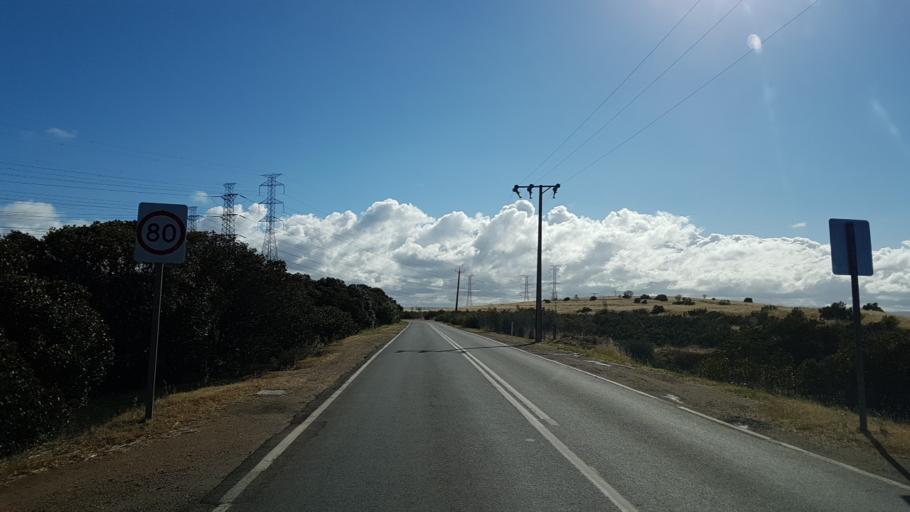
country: AU
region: South Australia
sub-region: Port Adelaide Enfield
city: Birkenhead
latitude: -34.8097
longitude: 138.5261
